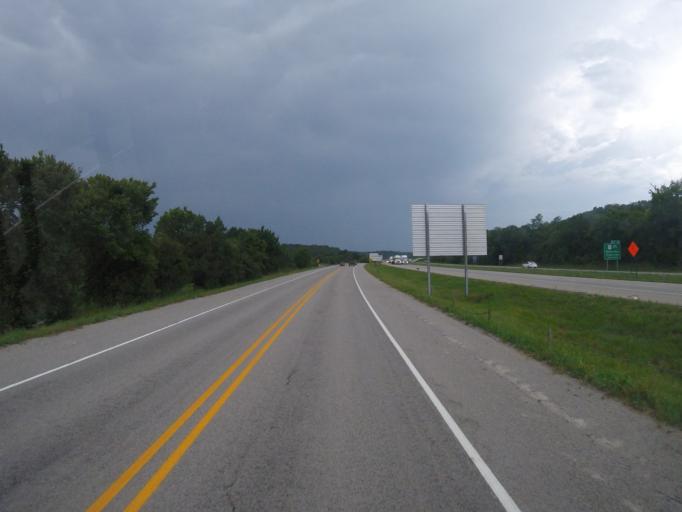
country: US
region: Arkansas
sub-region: Washington County
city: Fayetteville
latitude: 36.0487
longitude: -94.1914
